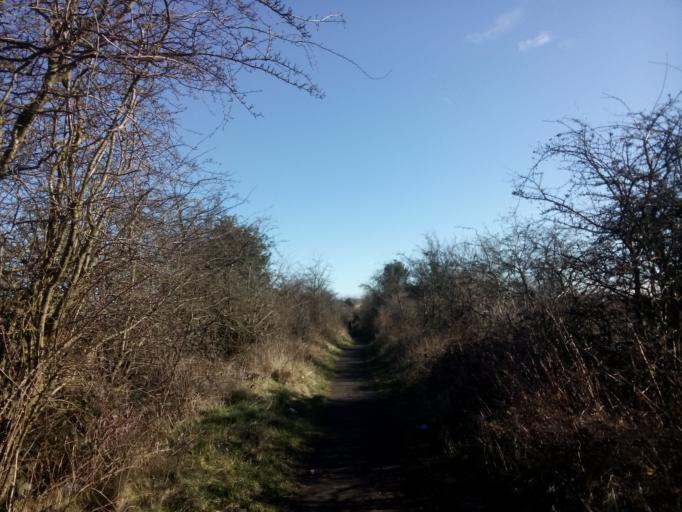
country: GB
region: England
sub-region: County Durham
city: Durham
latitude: 54.8001
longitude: -1.5880
